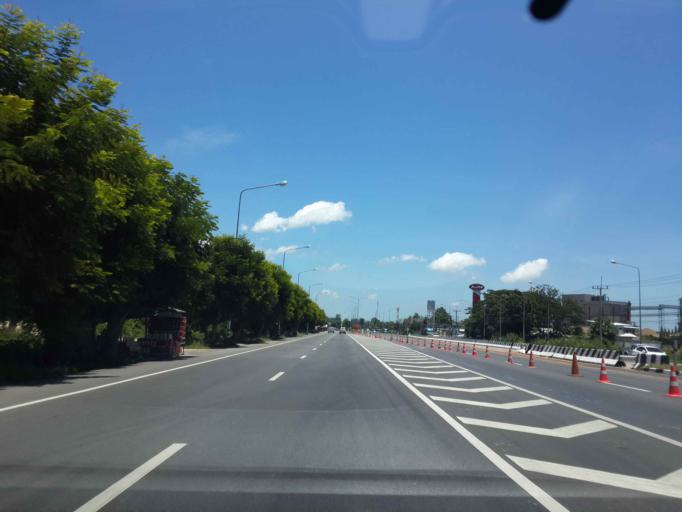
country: TH
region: Phetchaburi
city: Tha Yang
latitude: 12.9946
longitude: 99.9058
